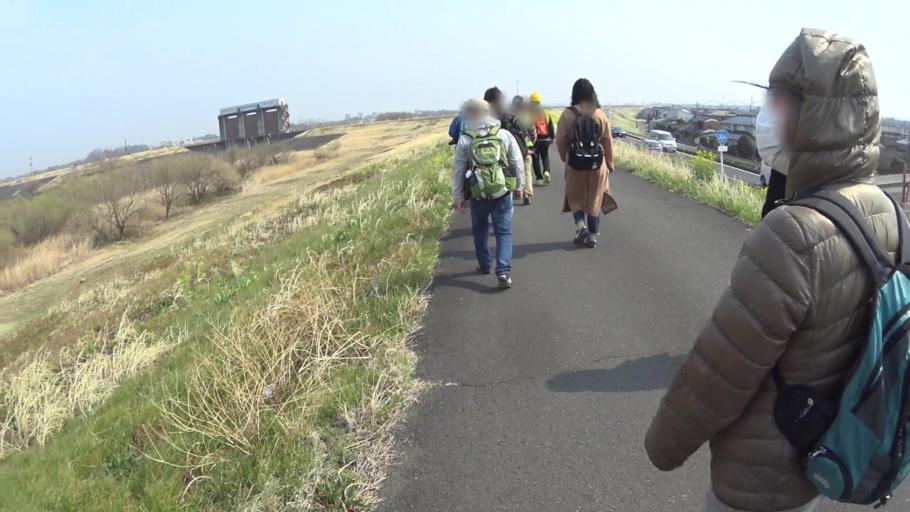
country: JP
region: Ibaraki
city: Koga
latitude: 36.1992
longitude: 139.6819
